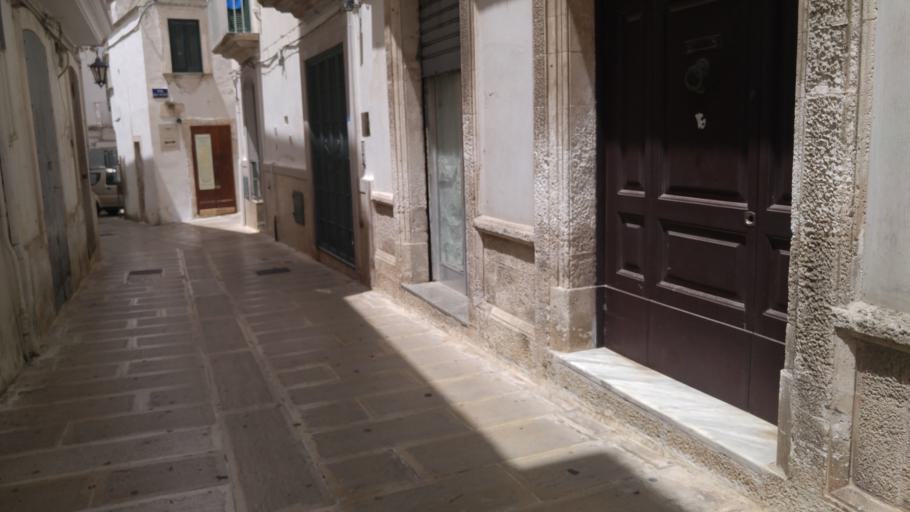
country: IT
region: Apulia
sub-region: Provincia di Taranto
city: Martina Franca
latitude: 40.7060
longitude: 17.3354
